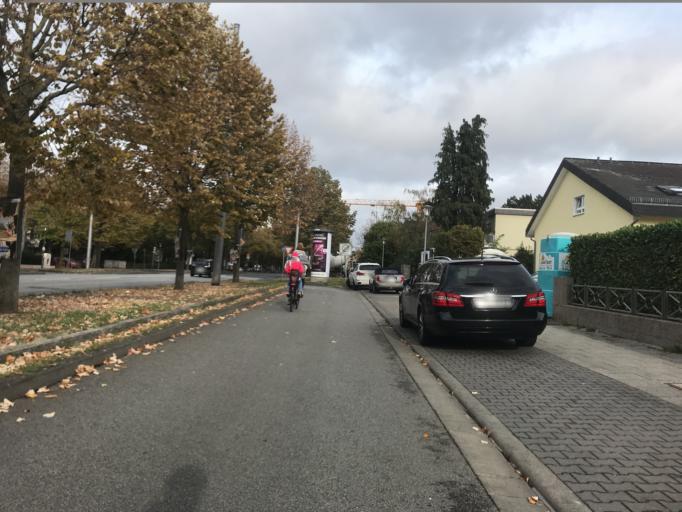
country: DE
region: Hesse
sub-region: Regierungsbezirk Darmstadt
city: Wiesbaden
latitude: 50.0560
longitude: 8.2438
